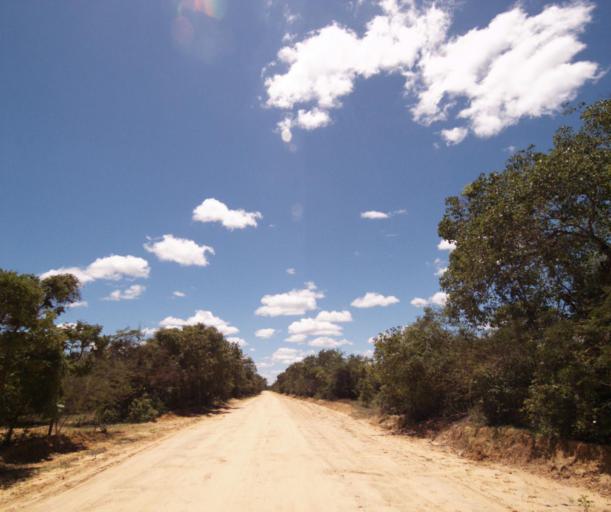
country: BR
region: Bahia
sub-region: Carinhanha
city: Carinhanha
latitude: -14.2116
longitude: -43.9285
